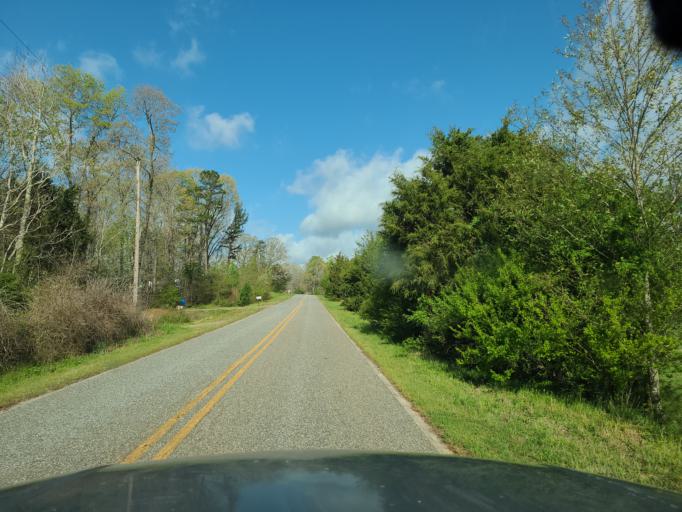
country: US
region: North Carolina
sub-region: Rutherford County
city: Forest City
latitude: 35.4280
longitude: -81.8256
